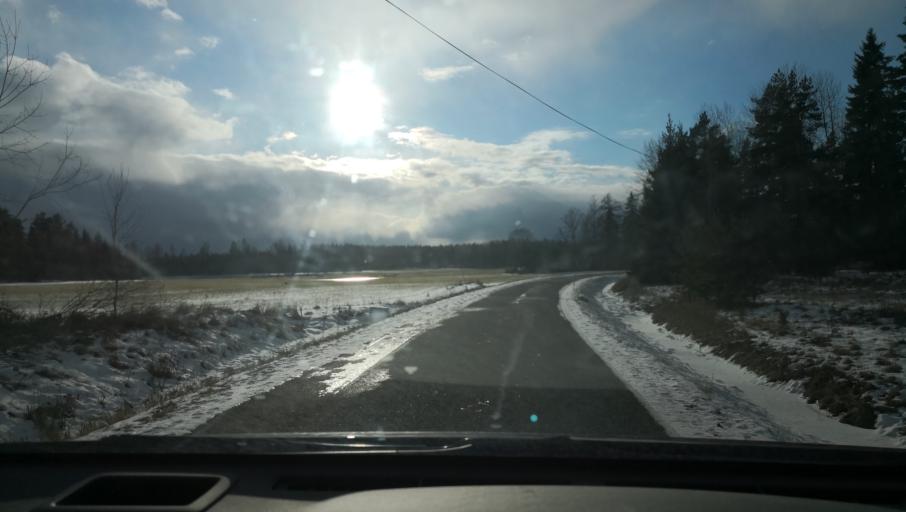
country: SE
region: Uppsala
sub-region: Enkopings Kommun
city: Irsta
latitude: 59.7056
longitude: 16.8856
